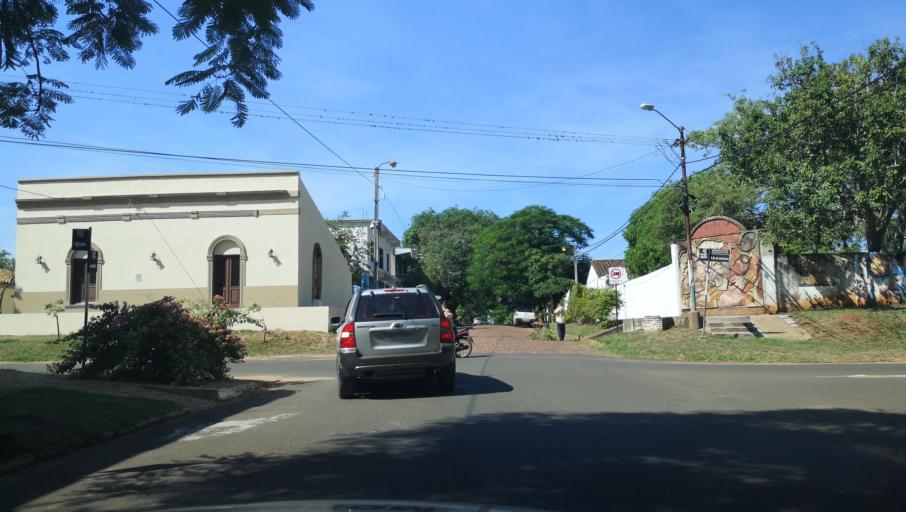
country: PY
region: Misiones
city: Santa Maria
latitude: -26.8897
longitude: -57.0234
